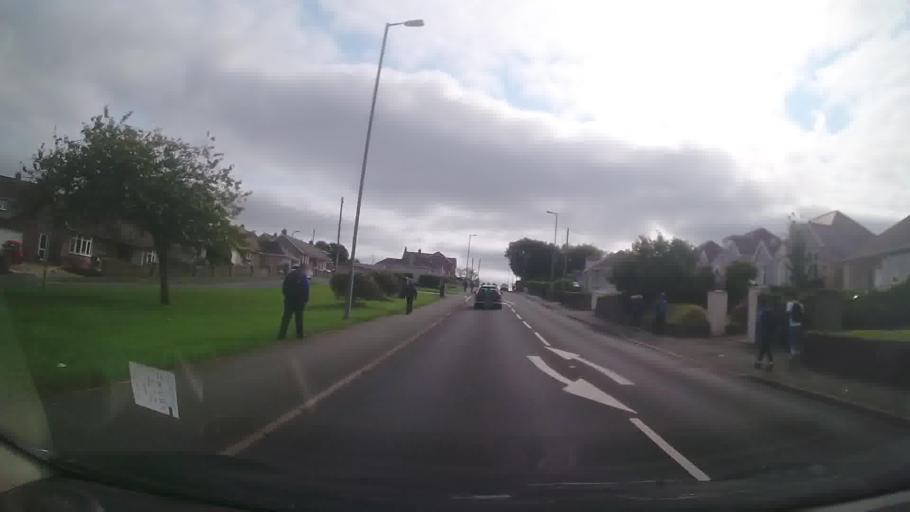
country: GB
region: Wales
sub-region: Pembrokeshire
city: Steynton
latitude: 51.7214
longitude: -5.0243
